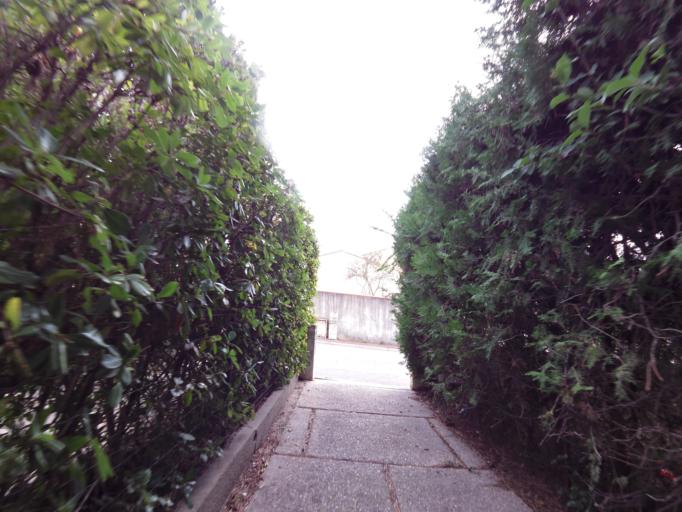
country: FR
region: Languedoc-Roussillon
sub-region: Departement du Gard
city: Vergeze
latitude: 43.7448
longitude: 4.2253
